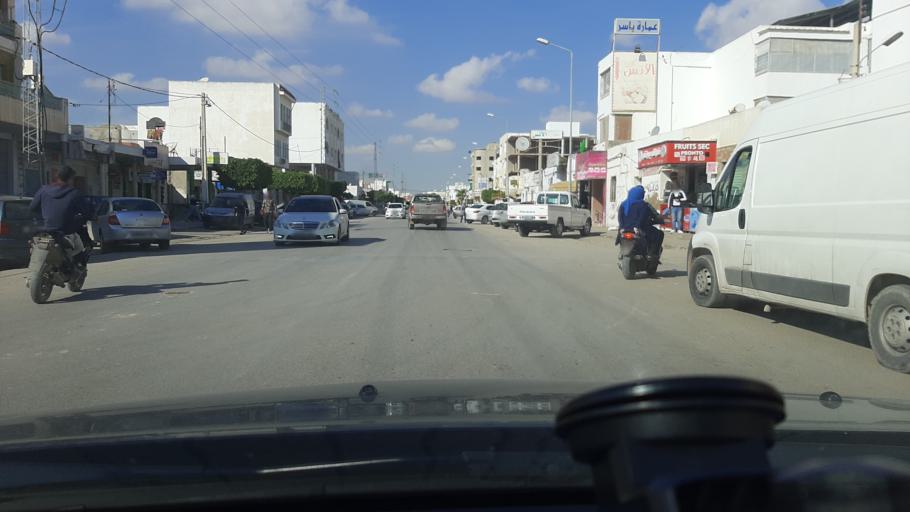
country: TN
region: Safaqis
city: Sfax
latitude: 34.7939
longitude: 10.7149
